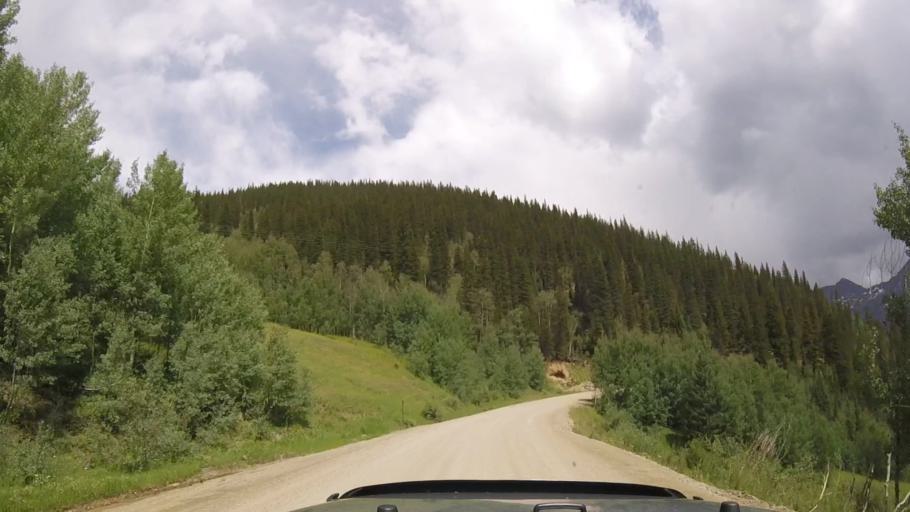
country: US
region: Colorado
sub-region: San Juan County
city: Silverton
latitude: 37.8339
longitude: -107.6732
